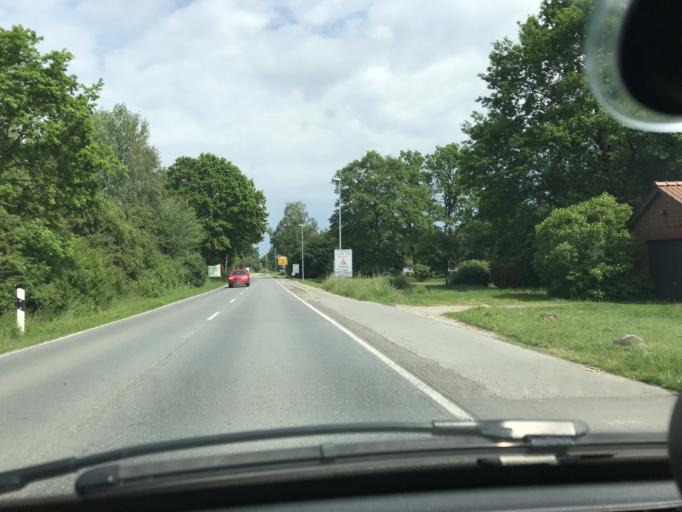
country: DE
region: Schleswig-Holstein
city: Trittau
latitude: 53.6149
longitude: 10.3895
